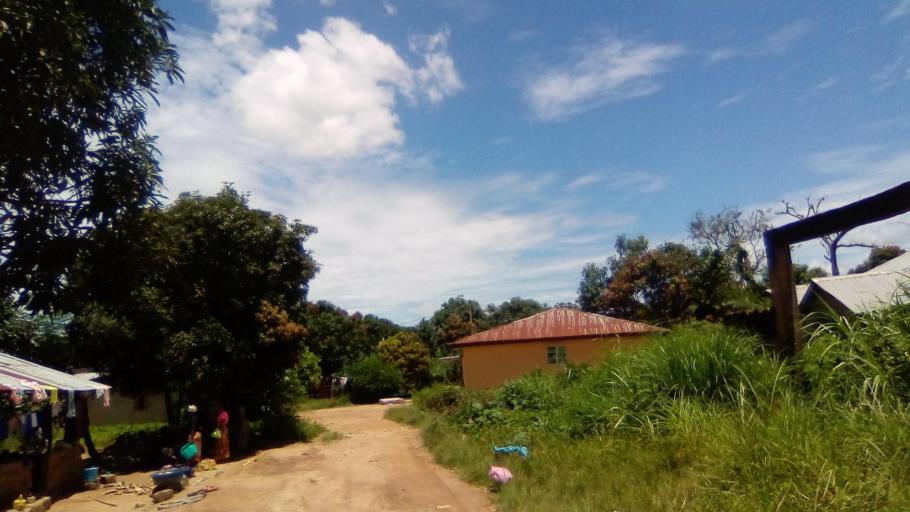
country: SL
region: Eastern Province
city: Simbakoro
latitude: 8.6255
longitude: -10.9880
